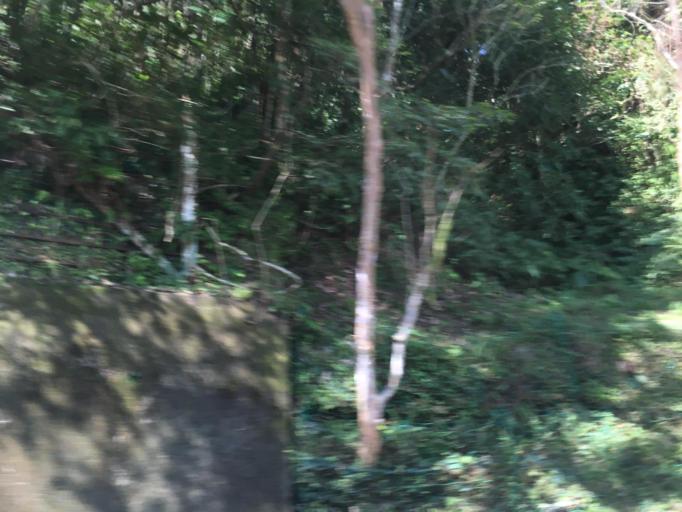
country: TW
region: Taiwan
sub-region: Yilan
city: Yilan
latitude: 24.7565
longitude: 121.5961
